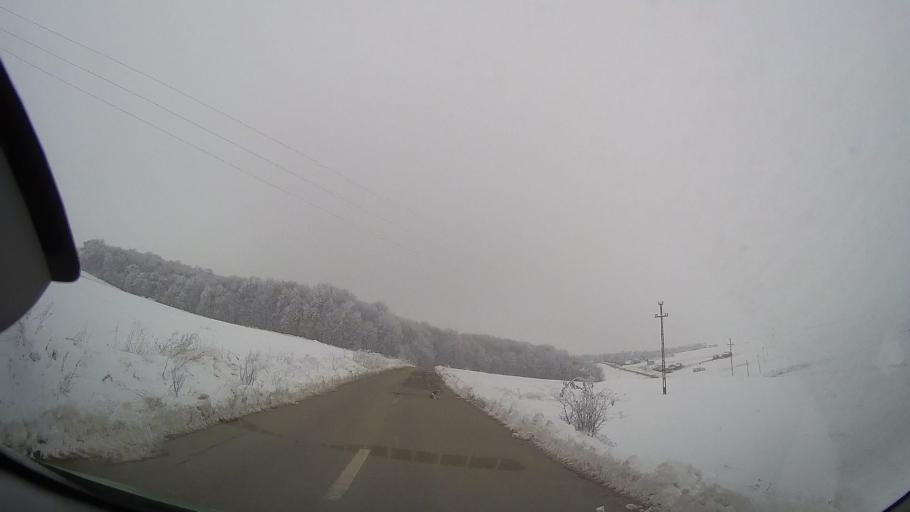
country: RO
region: Neamt
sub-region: Comuna Pancesti
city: Pancesti
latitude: 46.9155
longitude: 27.1627
